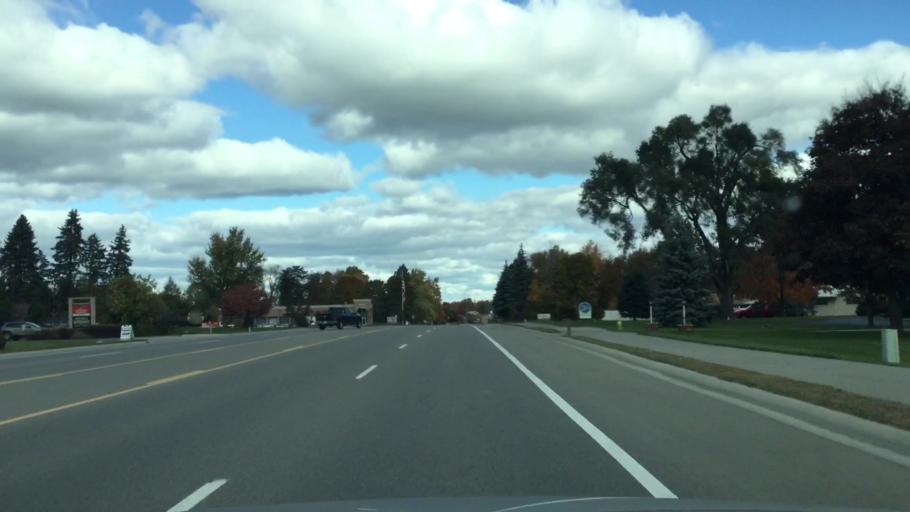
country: US
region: Michigan
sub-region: Lapeer County
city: Lapeer
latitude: 43.0317
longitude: -83.3227
